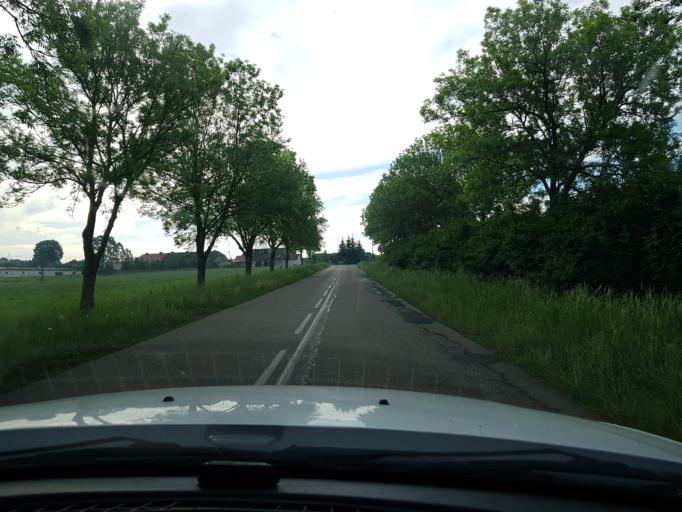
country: PL
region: West Pomeranian Voivodeship
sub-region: Powiat stargardzki
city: Chociwel
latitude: 53.4577
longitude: 15.3793
